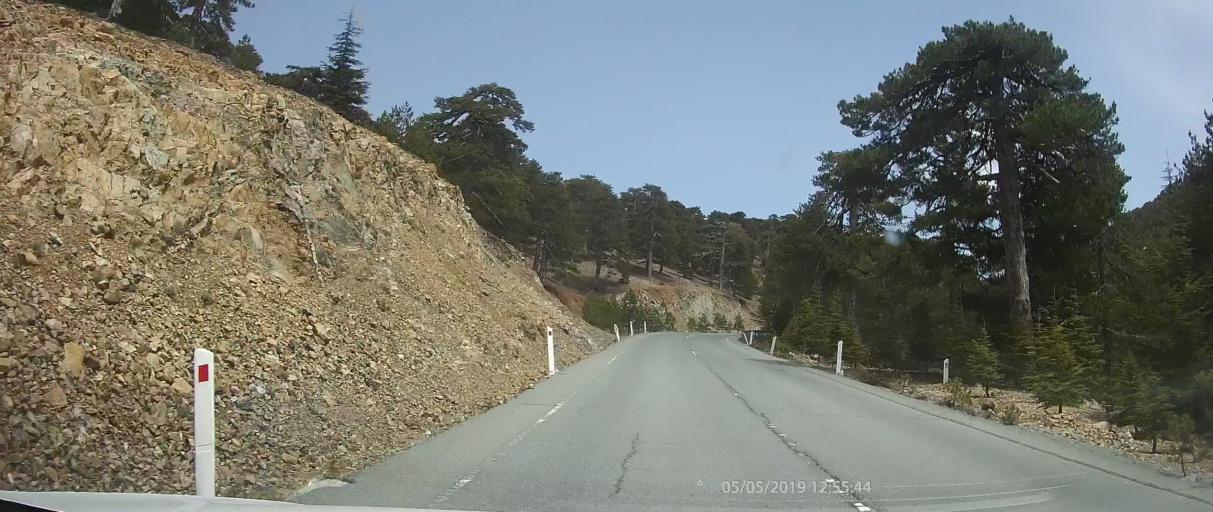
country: CY
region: Lefkosia
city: Kakopetria
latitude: 34.9437
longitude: 32.8559
